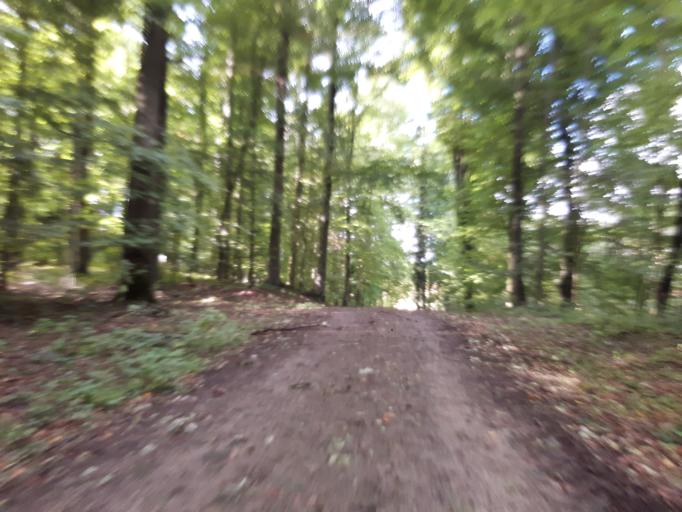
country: DE
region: Baden-Wuerttemberg
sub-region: Regierungsbezirk Stuttgart
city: Bad Rappenau
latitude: 49.2356
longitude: 9.1230
